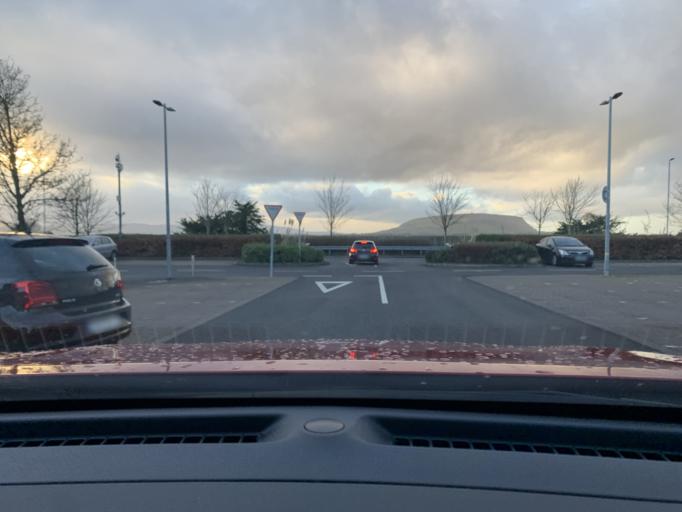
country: IE
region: Connaught
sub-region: Sligo
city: Sligo
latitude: 54.2500
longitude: -8.4721
